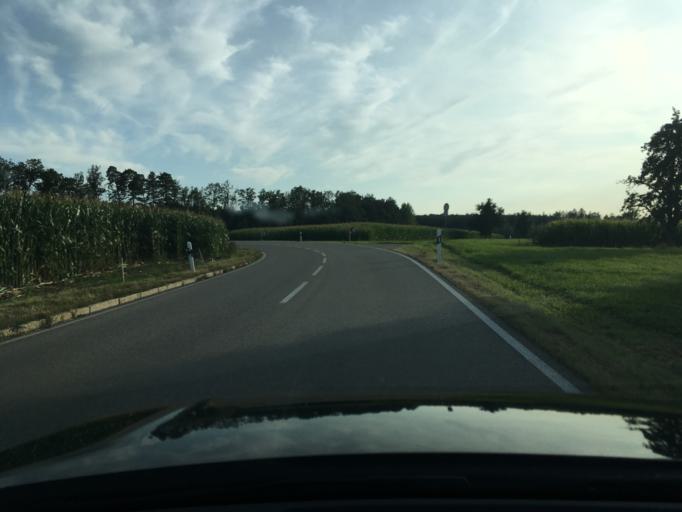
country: DE
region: Baden-Wuerttemberg
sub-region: Regierungsbezirk Stuttgart
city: Adelberg
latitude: 48.7587
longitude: 9.5638
